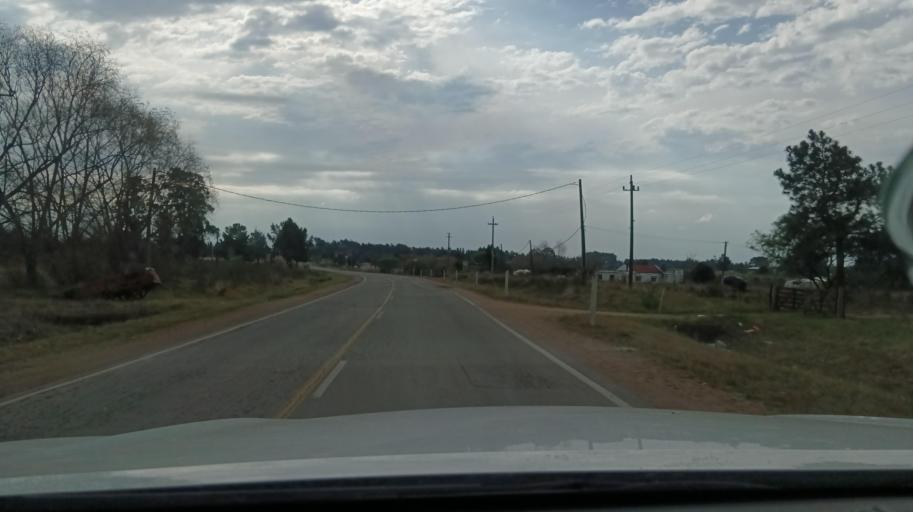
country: UY
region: Canelones
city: Sauce
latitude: -34.6794
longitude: -56.1121
